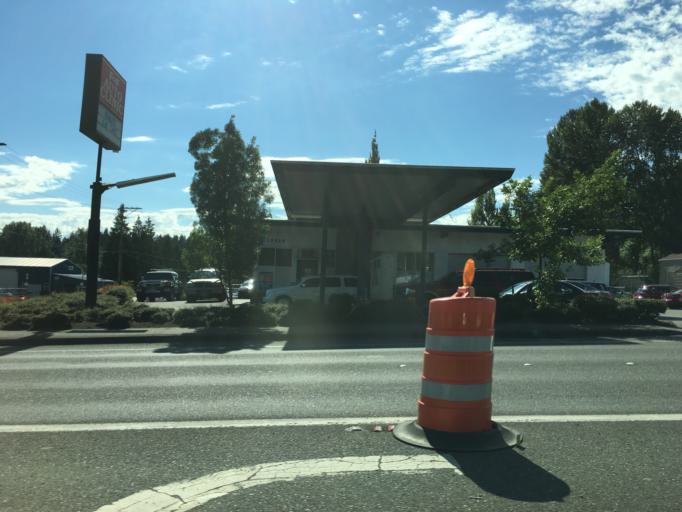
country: US
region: Washington
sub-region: Snohomish County
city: North Creek
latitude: 47.8205
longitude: -122.2074
